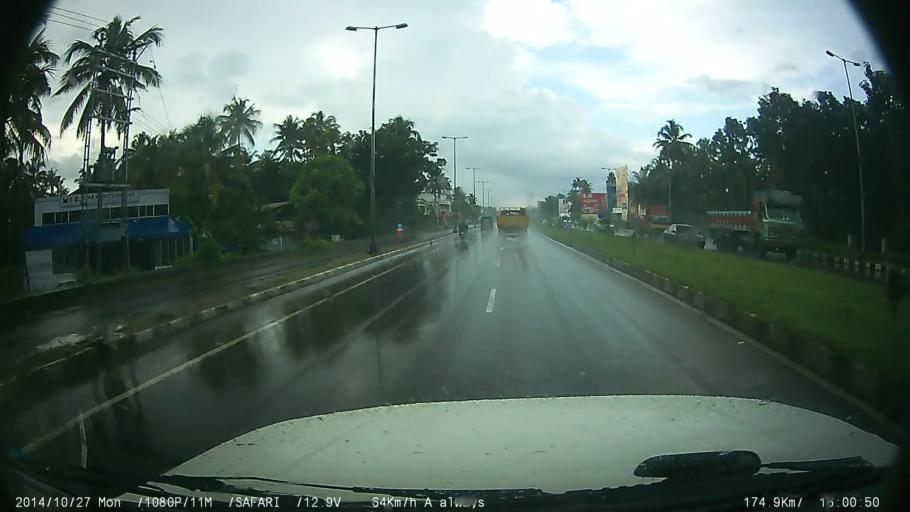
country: IN
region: Kerala
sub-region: Thrissur District
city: Kizhake Chalakudi
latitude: 10.3125
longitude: 76.3303
